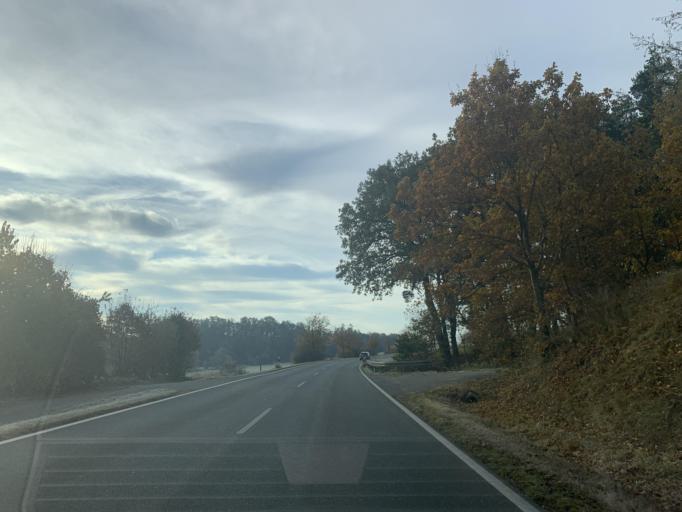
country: DE
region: Bavaria
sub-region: Upper Palatinate
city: Neunburg vorm Wald
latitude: 49.3663
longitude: 12.3785
